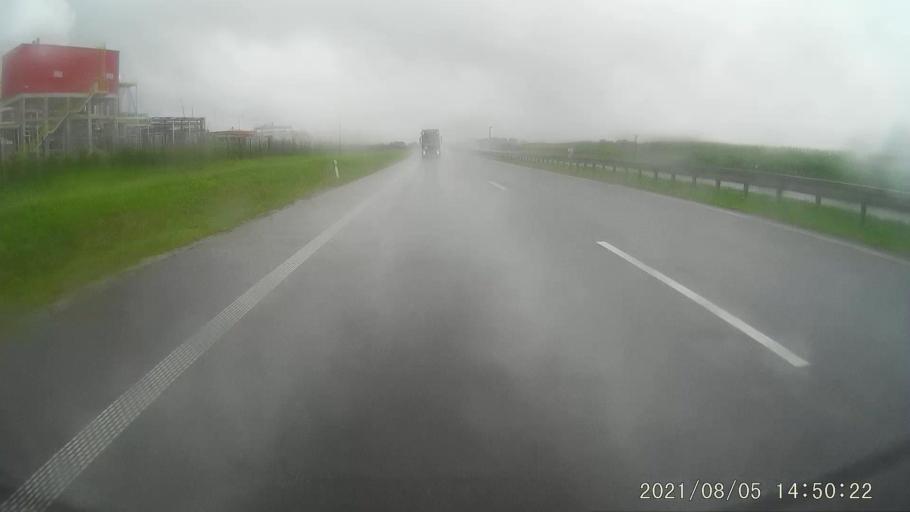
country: PL
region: Opole Voivodeship
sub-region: Powiat nyski
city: Nysa
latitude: 50.4799
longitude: 17.2649
